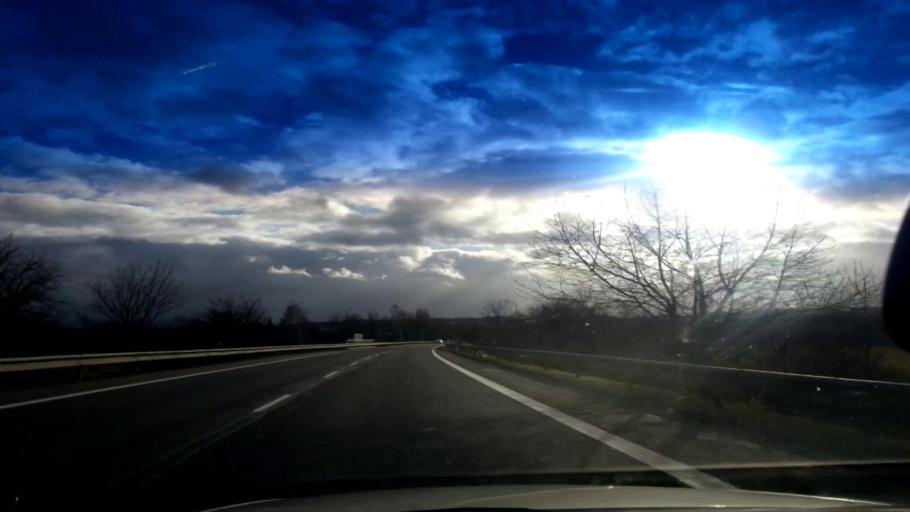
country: CZ
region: Karlovarsky
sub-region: Okres Cheb
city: Frantiskovy Lazne
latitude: 50.1165
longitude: 12.3732
